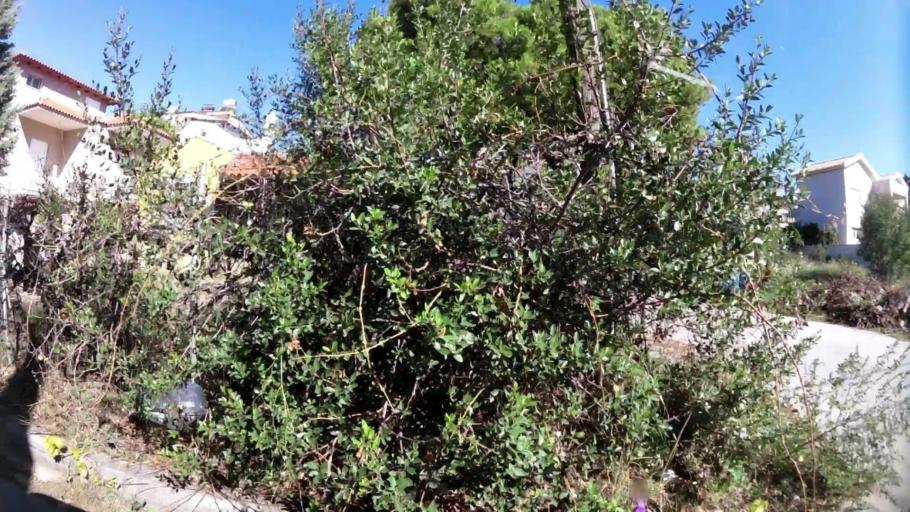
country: GR
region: Attica
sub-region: Nomarchia Athinas
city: Lykovrysi
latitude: 38.0876
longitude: 23.7901
